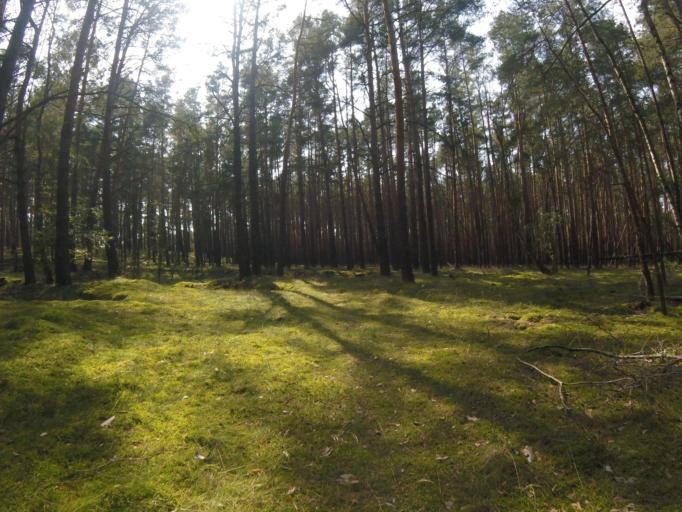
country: DE
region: Brandenburg
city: Bestensee
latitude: 52.2802
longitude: 13.7121
